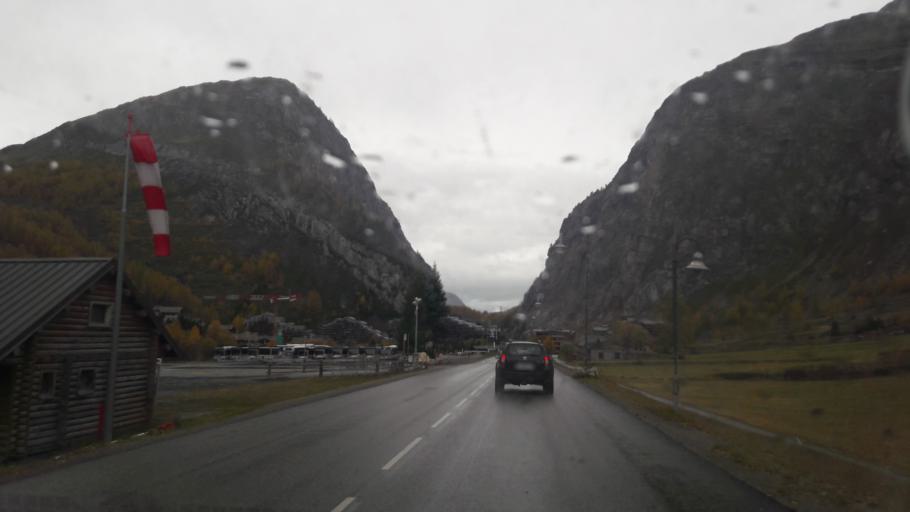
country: FR
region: Rhone-Alpes
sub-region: Departement de la Savoie
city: Val-d'Isere
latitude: 45.4572
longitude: 6.9682
